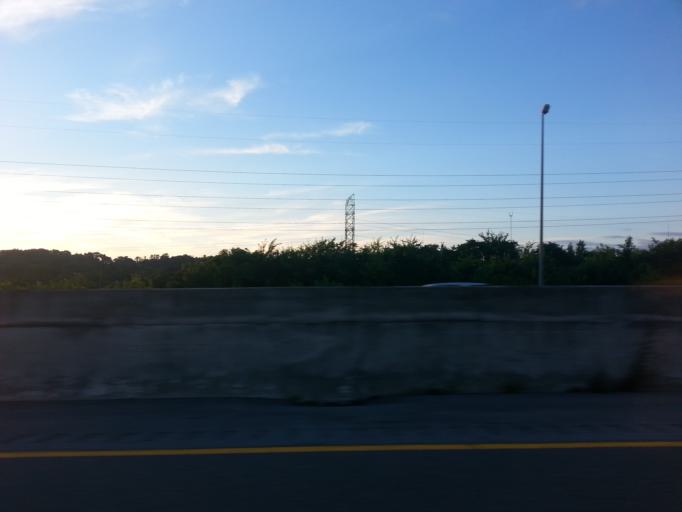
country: US
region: Tennessee
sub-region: Knox County
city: Knoxville
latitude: 35.9595
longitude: -83.9594
